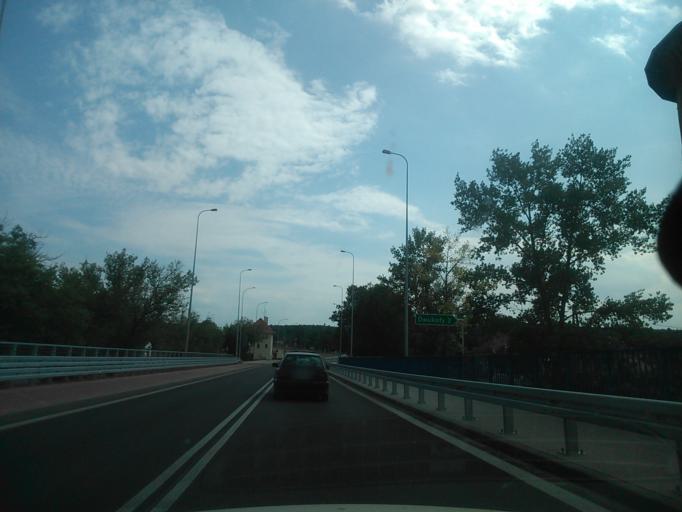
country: PL
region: Warmian-Masurian Voivodeship
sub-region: Powiat dzialdowski
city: Ilowo -Osada
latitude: 53.1651
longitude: 20.2934
